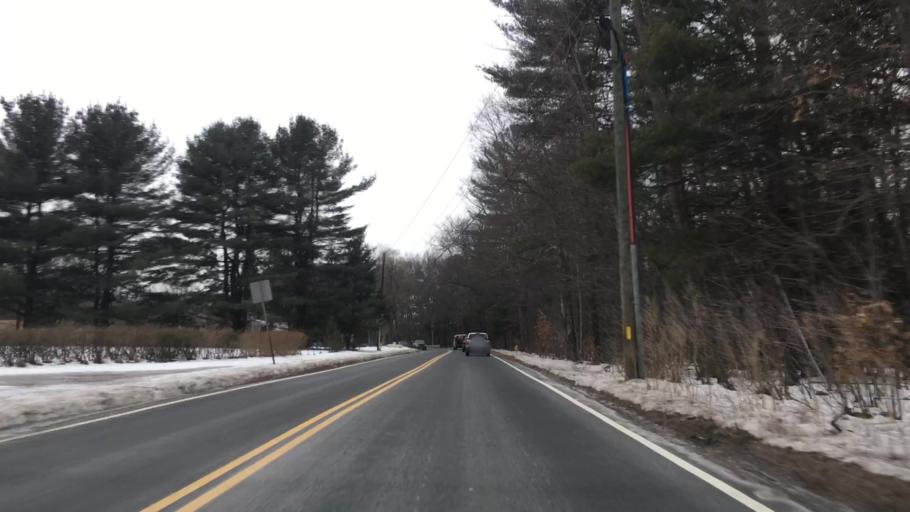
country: US
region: Massachusetts
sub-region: Hampden County
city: Westfield
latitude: 42.1034
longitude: -72.6917
